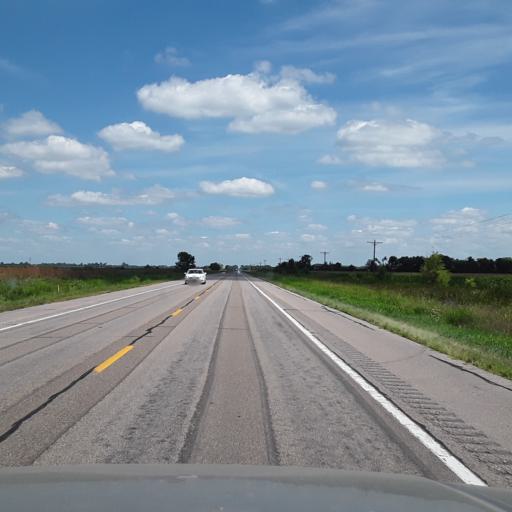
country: US
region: Nebraska
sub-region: Nance County
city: Genoa
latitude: 41.3331
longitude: -97.6231
